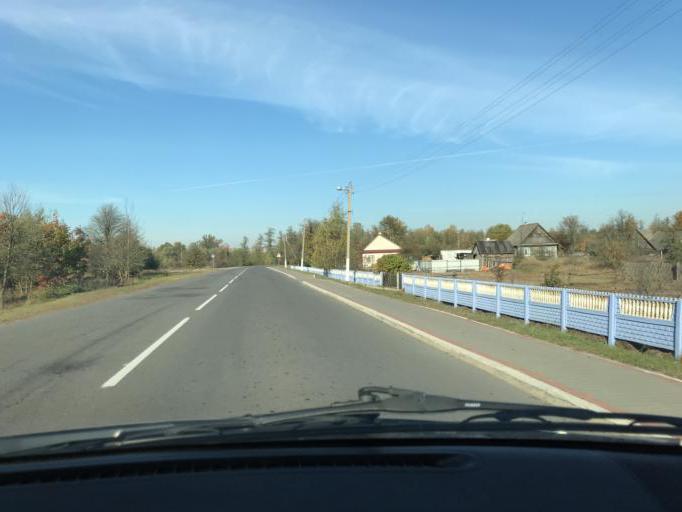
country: BY
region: Brest
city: Mikashevichy
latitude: 52.2315
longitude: 27.4517
